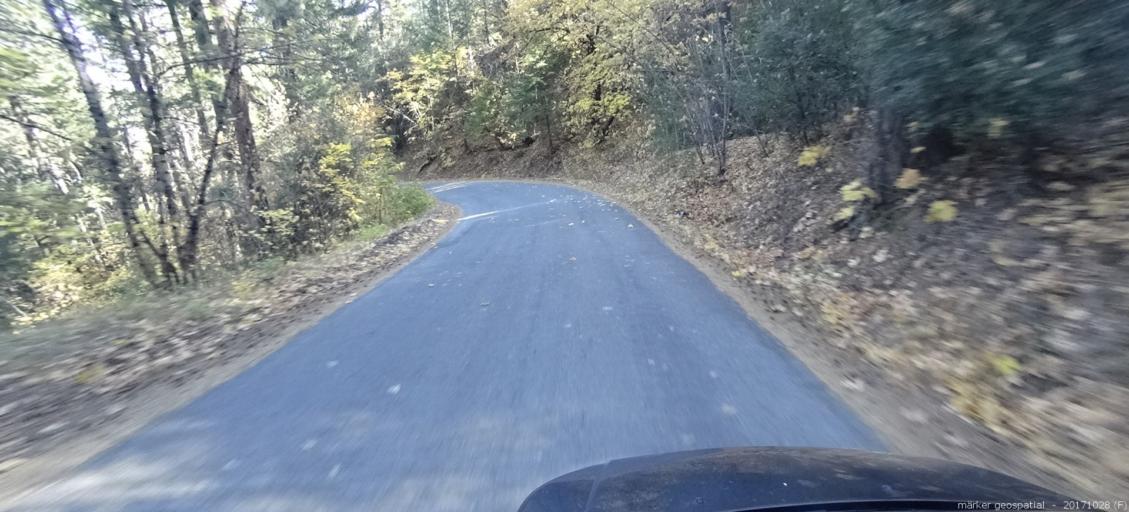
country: US
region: California
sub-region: Trinity County
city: Lewiston
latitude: 40.8142
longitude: -122.6408
